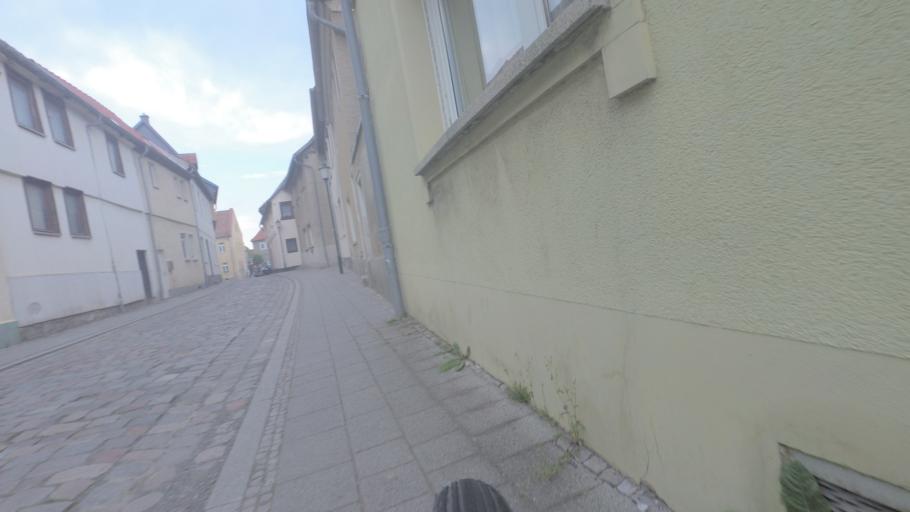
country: DE
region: Saxony-Anhalt
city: Hoym
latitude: 51.7304
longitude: 11.3440
